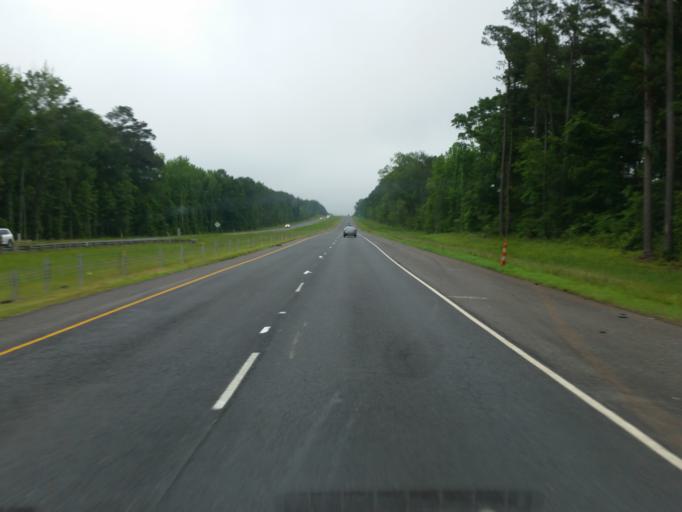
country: US
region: Louisiana
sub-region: Bienville Parish
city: Arcadia
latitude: 32.5633
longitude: -93.0844
